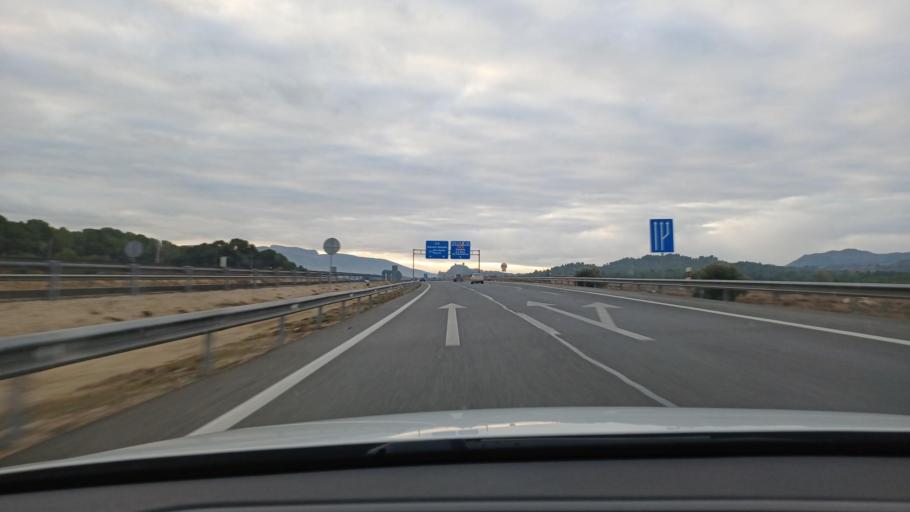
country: ES
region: Valencia
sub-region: Provincia de Alicante
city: Sax
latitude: 38.5650
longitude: -0.8338
